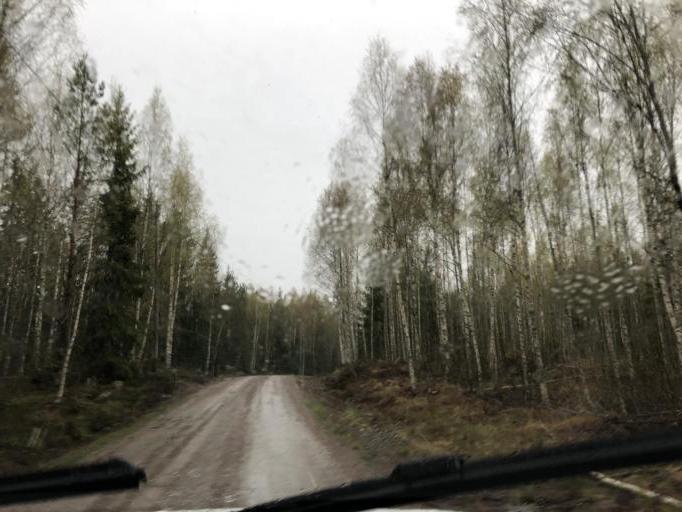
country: SE
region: Uppsala
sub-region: Heby Kommun
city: Tarnsjo
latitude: 60.2004
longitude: 16.8918
